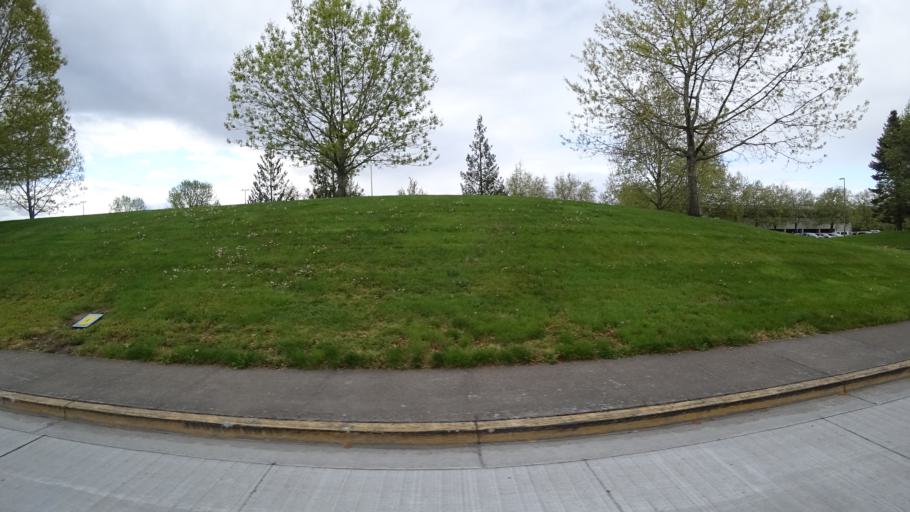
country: US
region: Oregon
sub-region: Washington County
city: Hillsboro
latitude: 45.5401
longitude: -122.9617
